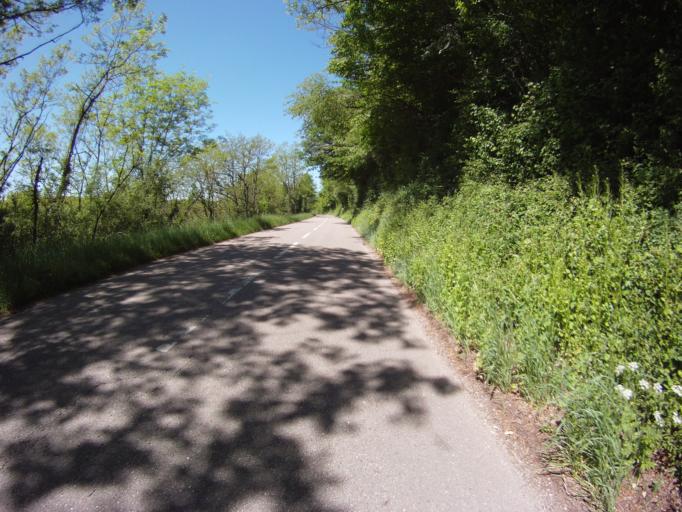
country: FR
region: Lorraine
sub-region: Departement de Meurthe-et-Moselle
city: Dommartin-les-Toul
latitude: 48.6468
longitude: 5.9307
